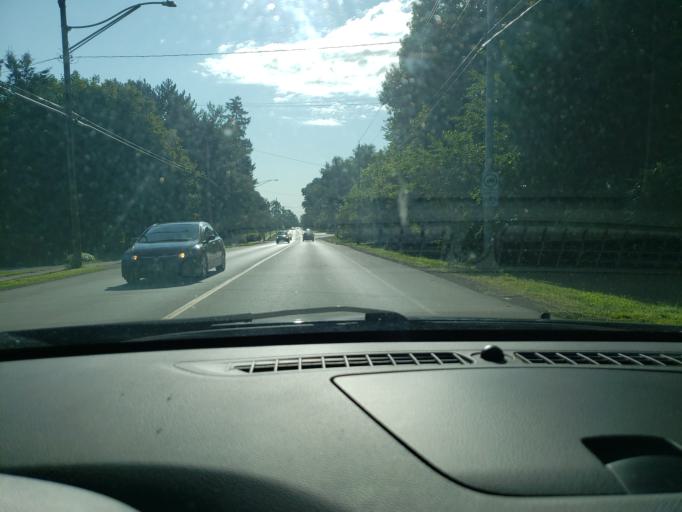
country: CA
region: Ontario
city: Hamilton
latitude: 43.1945
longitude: -79.5934
